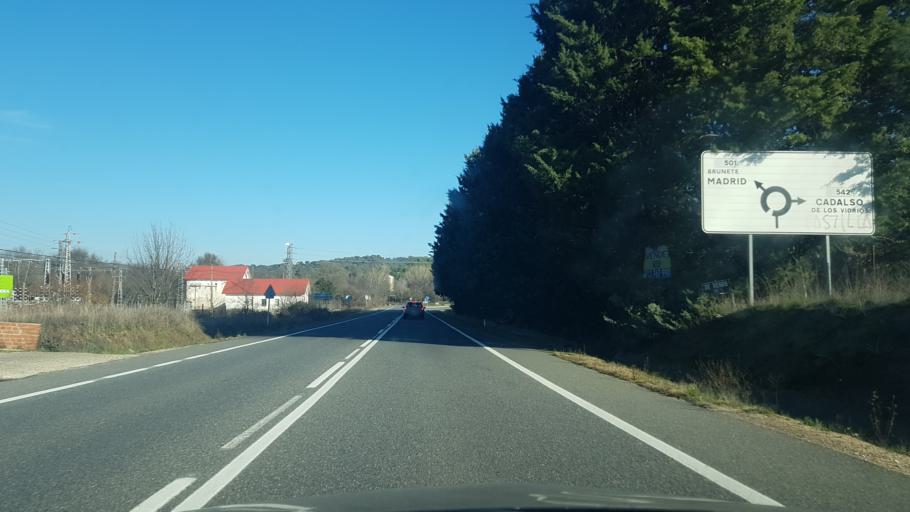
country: ES
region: Madrid
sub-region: Provincia de Madrid
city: Cadalso de los Vidrios
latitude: 40.3453
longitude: -4.4466
